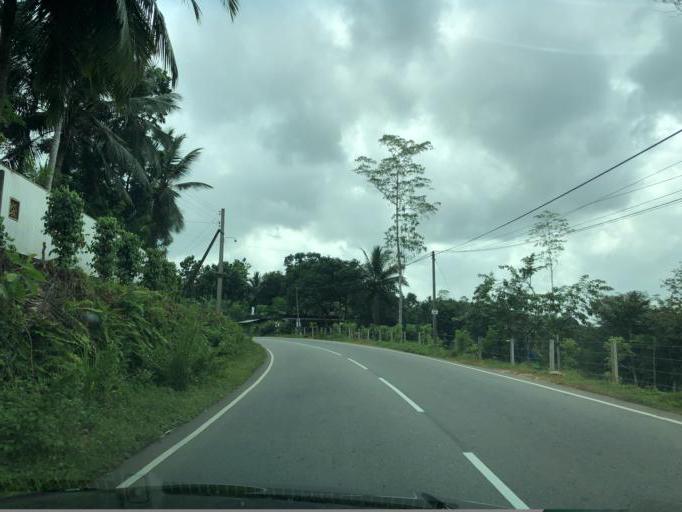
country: LK
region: Western
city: Horana South
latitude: 6.6938
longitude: 80.1398
